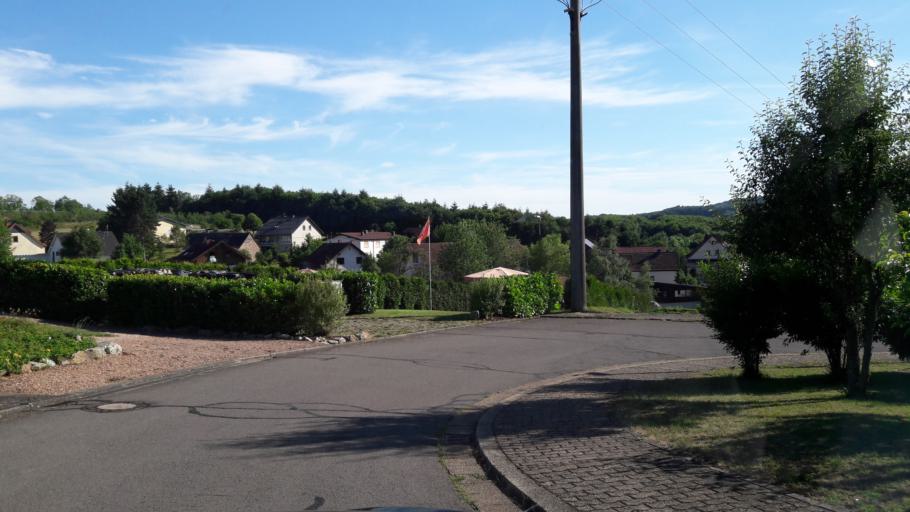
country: DE
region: Rheinland-Pfalz
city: Achtelsbach
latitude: 49.5774
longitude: 7.0690
